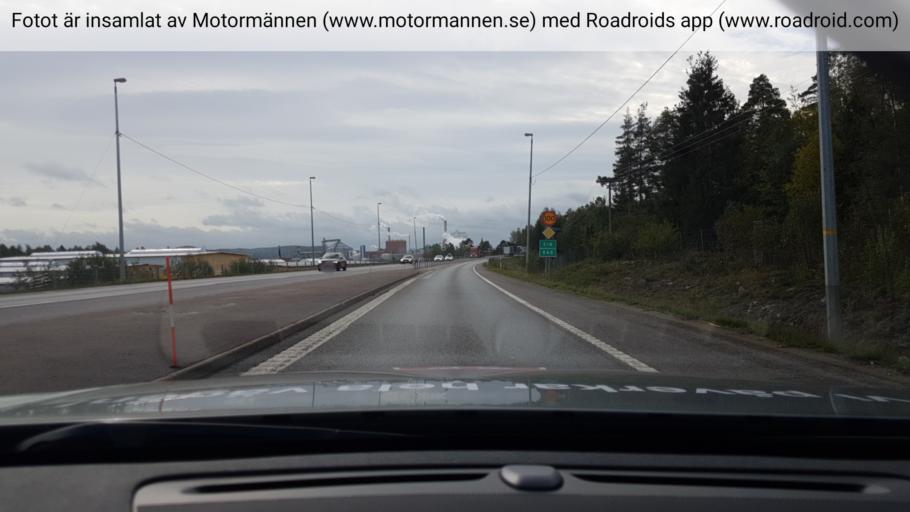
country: SE
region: Vaermland
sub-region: Grums Kommun
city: Grums
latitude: 59.3536
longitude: 13.1300
